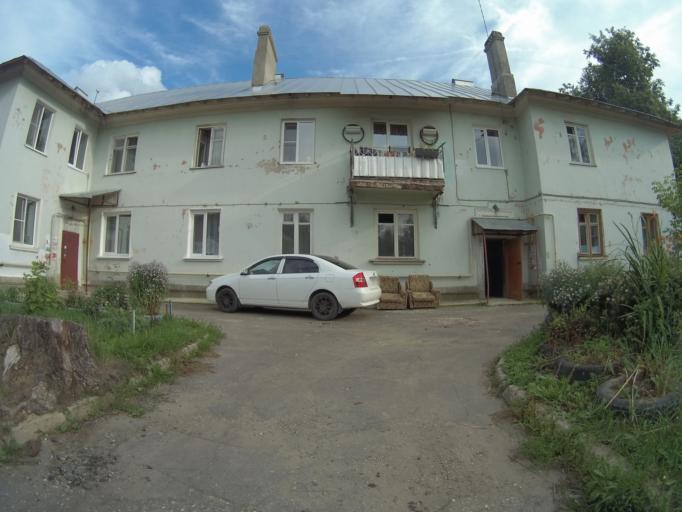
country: RU
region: Vladimir
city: Vladimir
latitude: 56.1458
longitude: 40.4306
